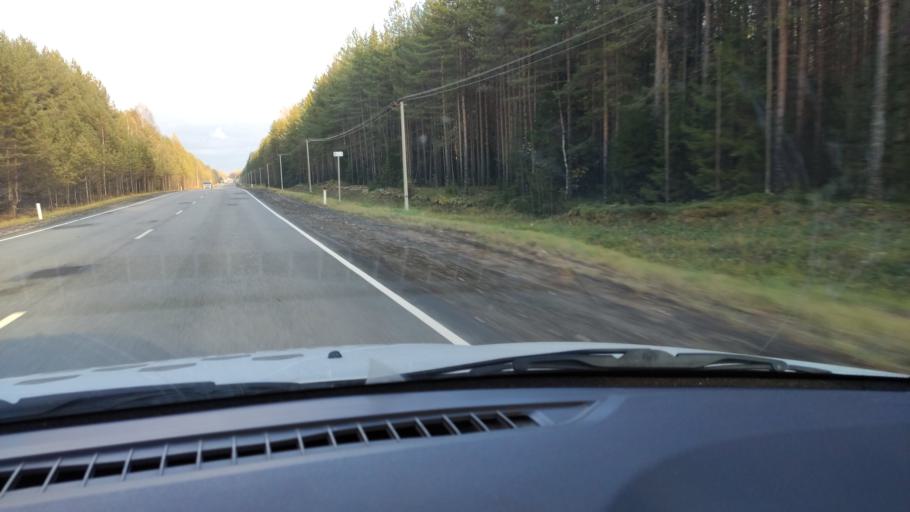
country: RU
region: Kirov
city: Belaya Kholunitsa
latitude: 58.9090
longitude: 51.0535
